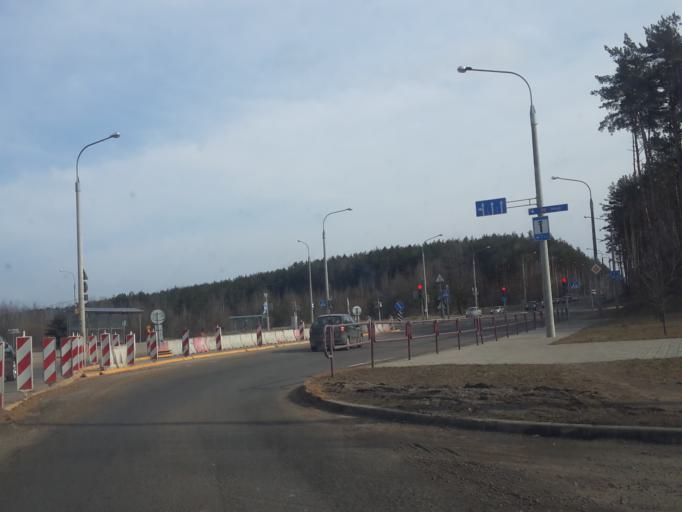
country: BY
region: Minsk
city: Vyaliki Trastsyanets
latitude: 53.9016
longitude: 27.6636
